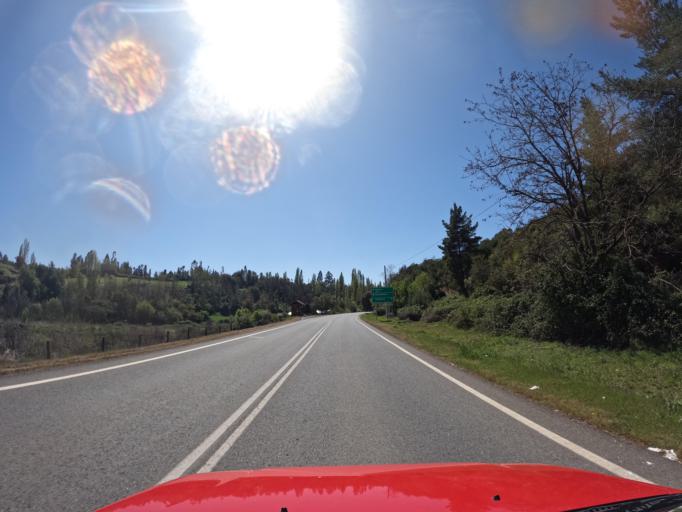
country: CL
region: Maule
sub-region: Provincia de Talca
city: San Clemente
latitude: -35.4618
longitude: -71.2694
